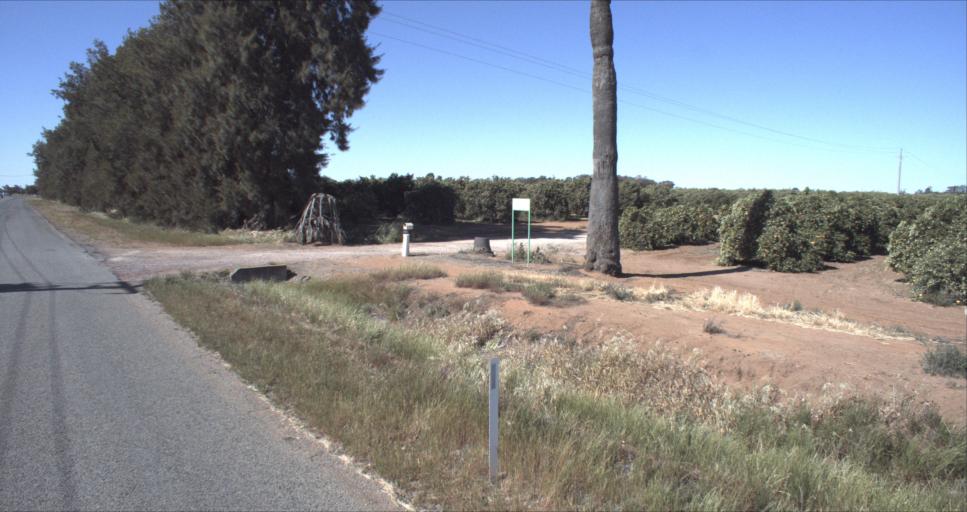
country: AU
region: New South Wales
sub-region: Leeton
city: Leeton
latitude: -34.5670
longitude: 146.3824
